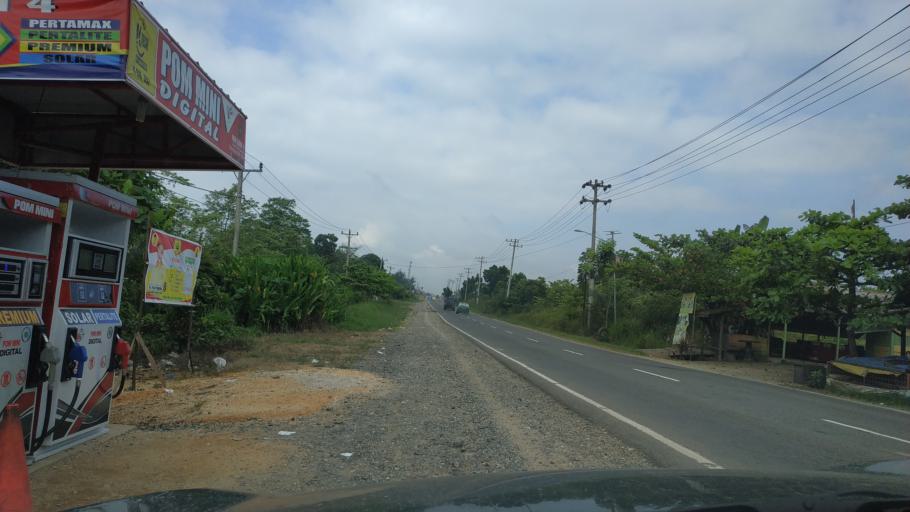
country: ID
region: Riau
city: Rengat
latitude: -0.3963
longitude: 102.4277
